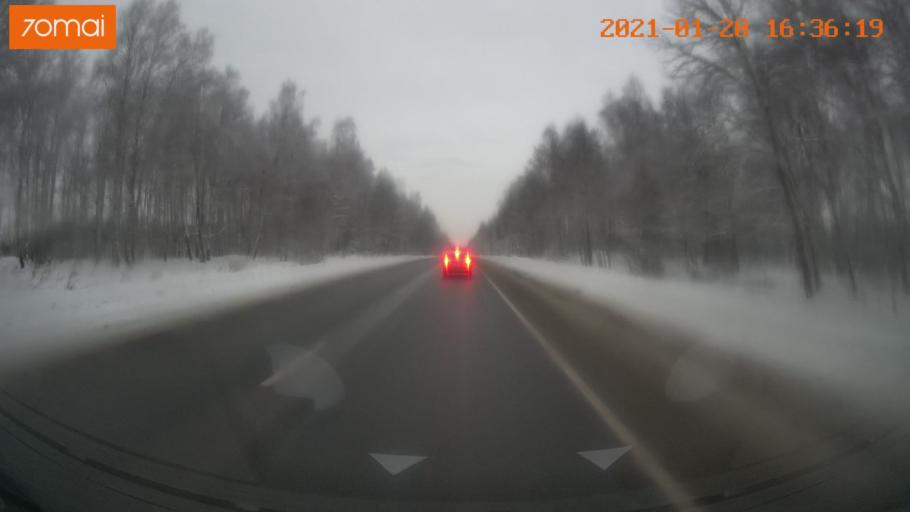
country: RU
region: Vladimir
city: Orgtrud
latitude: 56.2042
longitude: 40.7400
